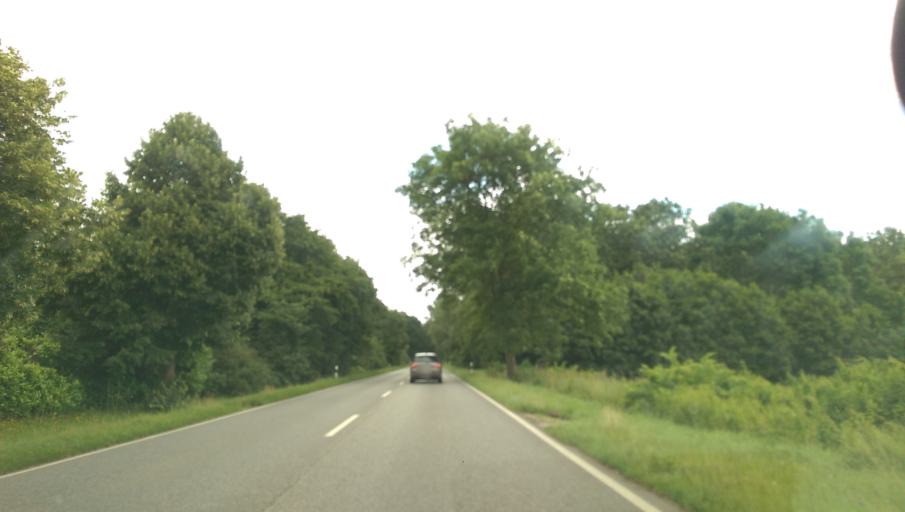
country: DE
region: Schleswig-Holstein
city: Timmendorfer Strand
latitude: 53.9883
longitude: 10.7963
